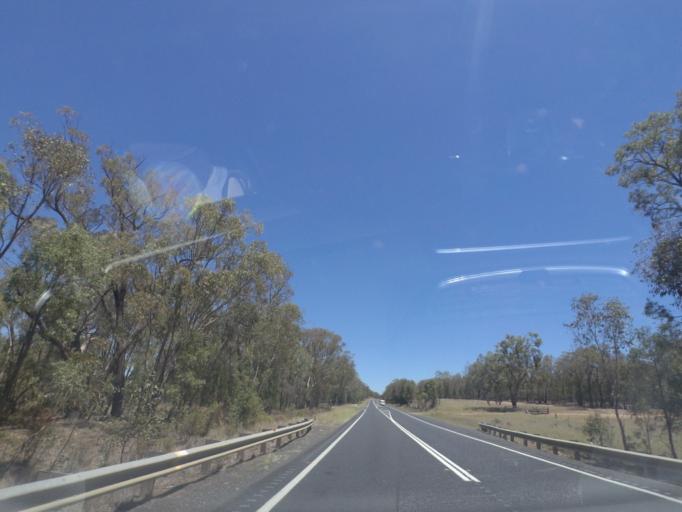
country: AU
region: New South Wales
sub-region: Warrumbungle Shire
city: Coonabarabran
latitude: -31.2248
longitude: 149.3229
